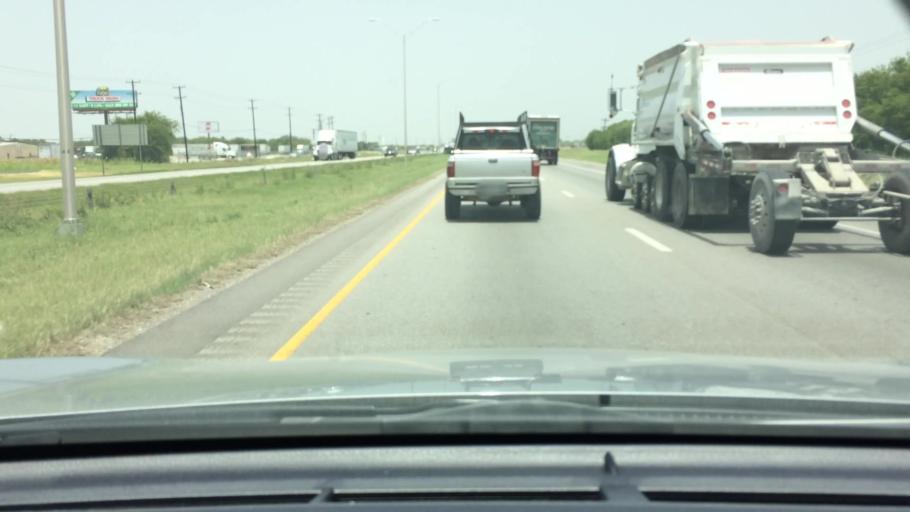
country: US
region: Texas
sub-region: Bexar County
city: Kirby
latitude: 29.4171
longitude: -98.3892
